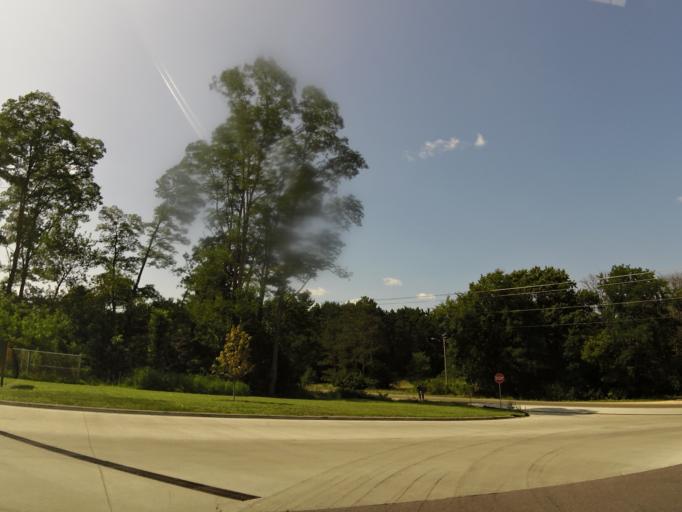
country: US
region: Wisconsin
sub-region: Columbia County
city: Poynette
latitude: 43.3894
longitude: -89.4717
